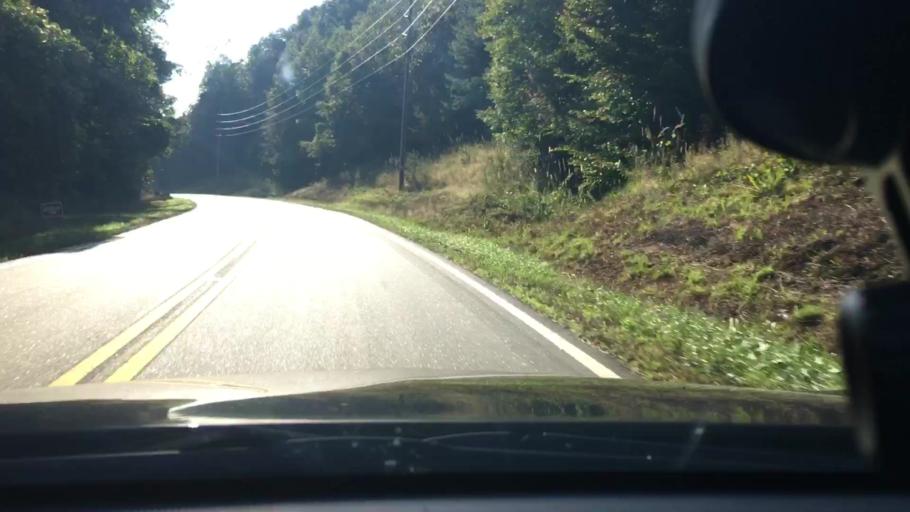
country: US
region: North Carolina
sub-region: Polk County
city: Columbus
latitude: 35.3228
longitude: -82.0879
